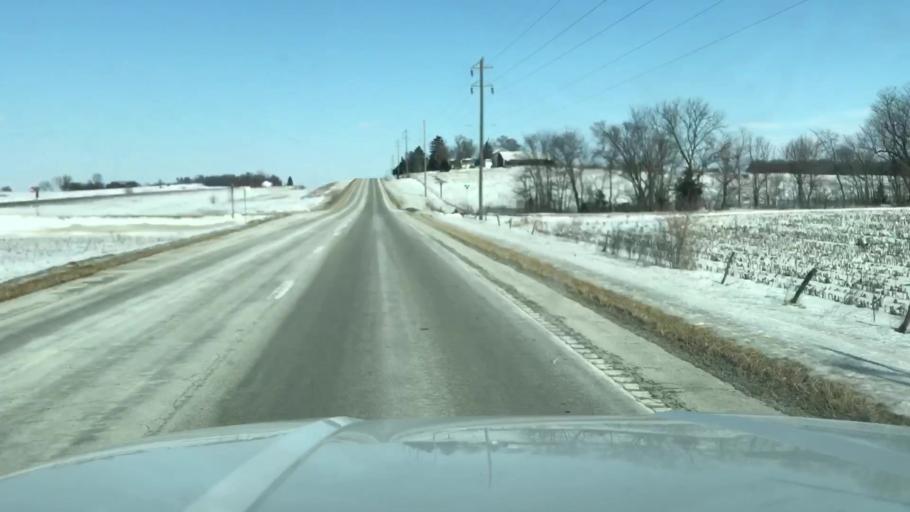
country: US
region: Missouri
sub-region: Nodaway County
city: Maryville
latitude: 40.1488
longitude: -94.8691
